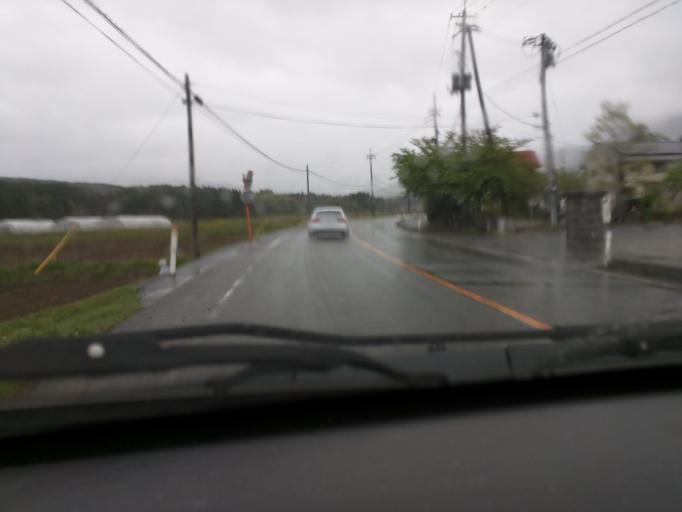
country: JP
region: Fukushima
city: Inawashiro
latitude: 37.5714
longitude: 140.1162
